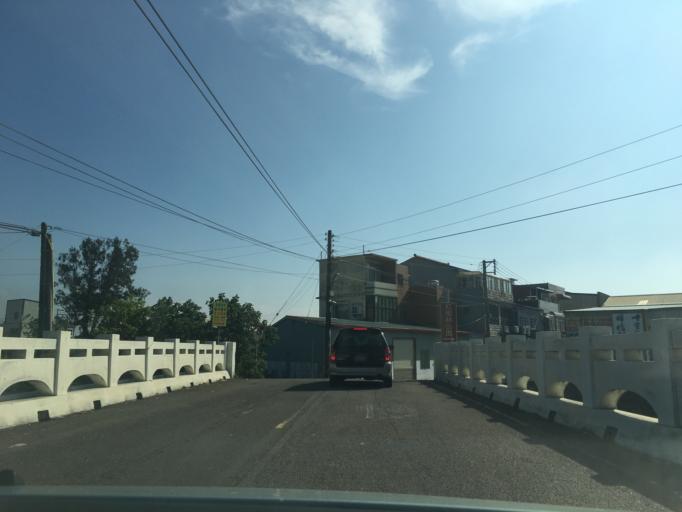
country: TW
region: Taiwan
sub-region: Hsinchu
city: Hsinchu
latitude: 24.8108
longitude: 120.9217
